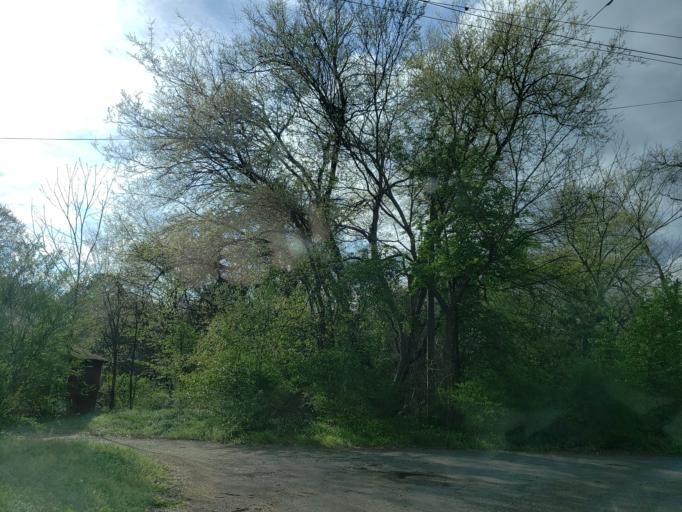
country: US
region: Georgia
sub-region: Bartow County
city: Emerson
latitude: 34.1258
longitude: -84.7608
